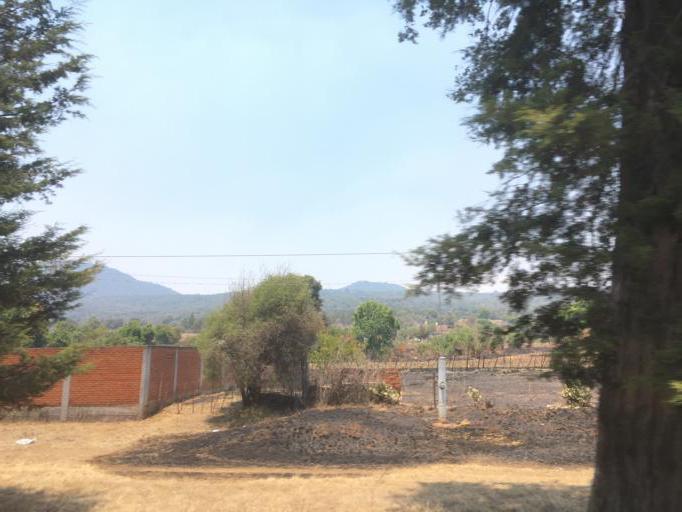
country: MX
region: Michoacan
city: Quiroga
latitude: 19.6440
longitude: -101.4897
